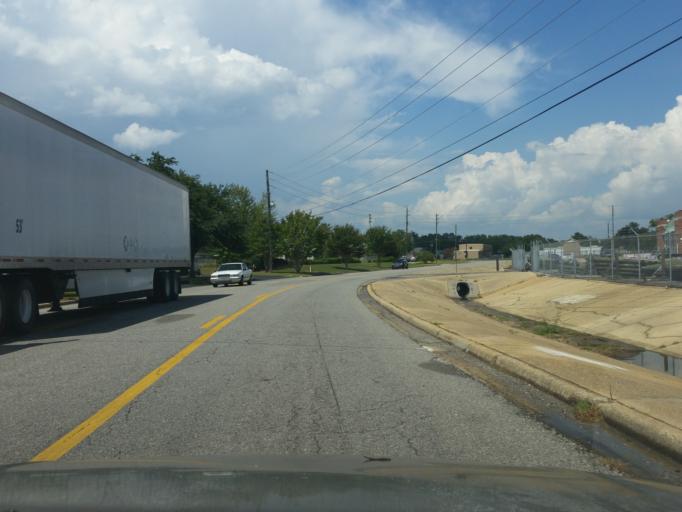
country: US
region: Florida
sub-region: Escambia County
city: Ferry Pass
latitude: 30.5255
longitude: -87.2014
